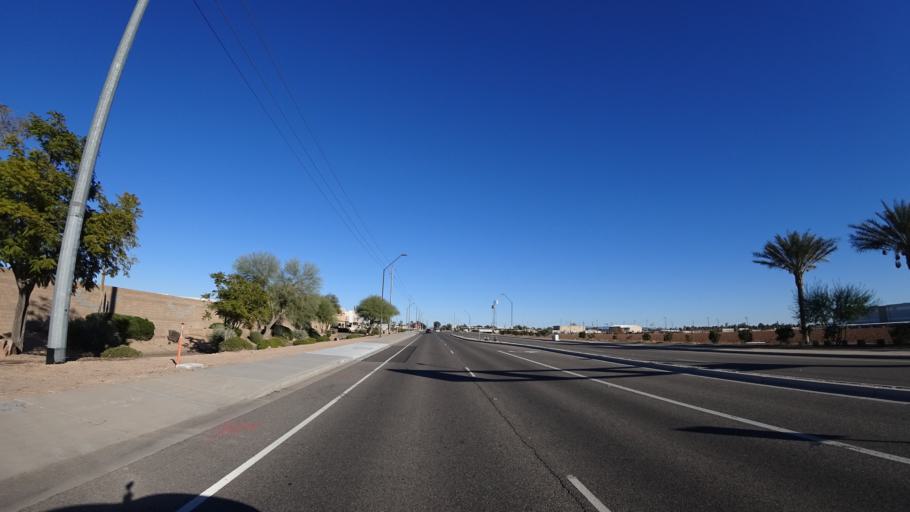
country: US
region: Arizona
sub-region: Maricopa County
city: Goodyear
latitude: 33.4499
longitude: -112.3664
